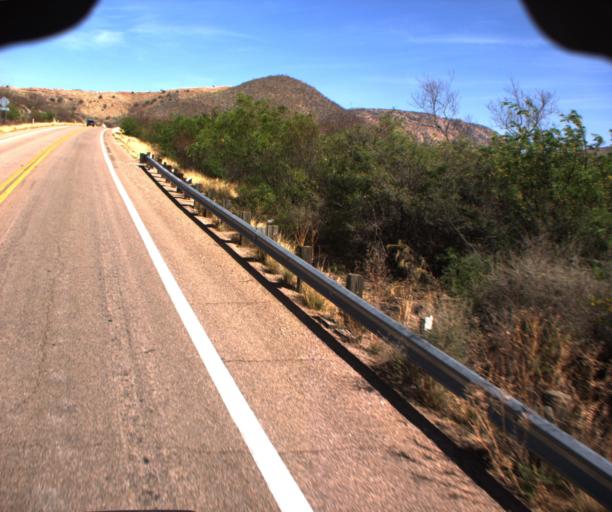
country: US
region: Arizona
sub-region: Cochise County
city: Bisbee
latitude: 31.5173
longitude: -110.0251
